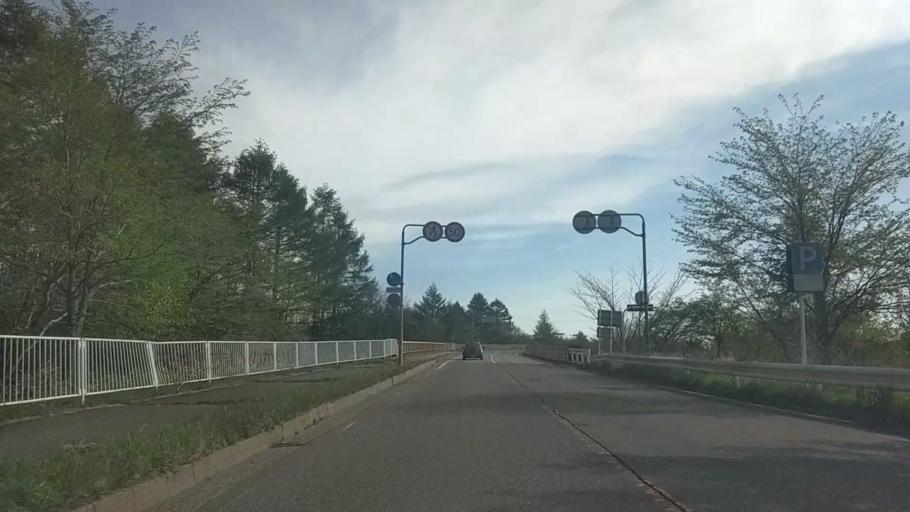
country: JP
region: Yamanashi
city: Nirasaki
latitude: 35.9427
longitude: 138.4506
